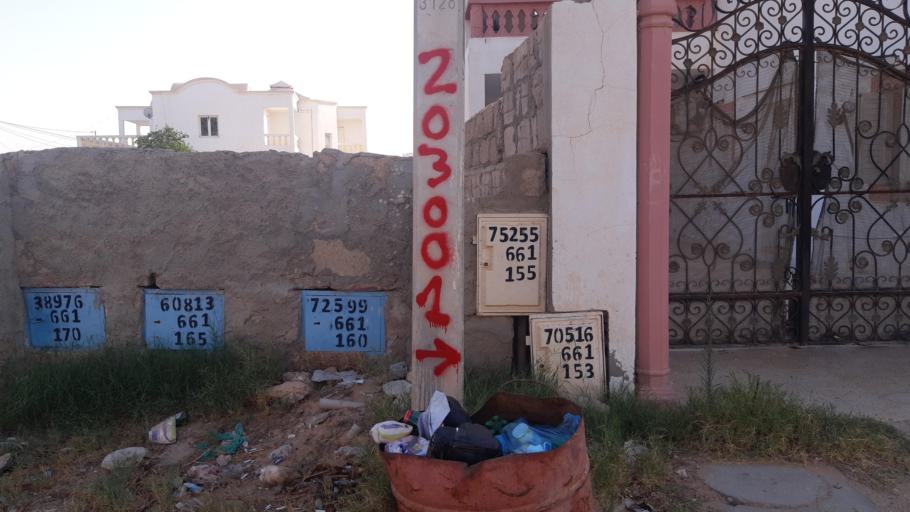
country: TN
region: Madanin
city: Bin Qirdan
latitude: 33.1250
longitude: 11.2286
